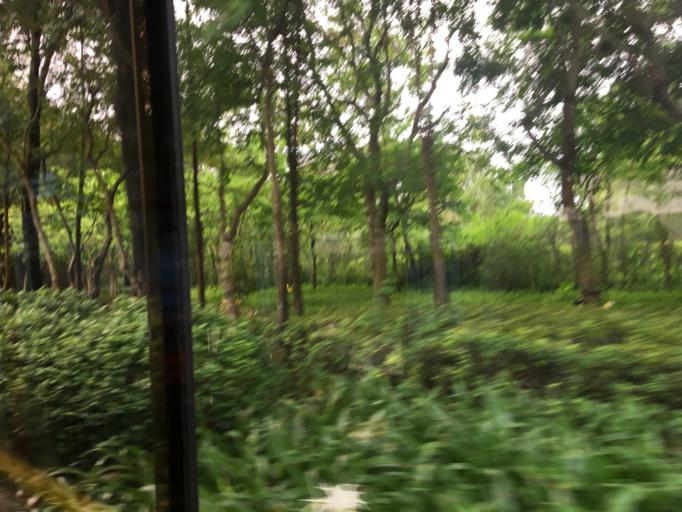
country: CN
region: Guangdong
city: Shahe
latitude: 22.5286
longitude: 113.9769
